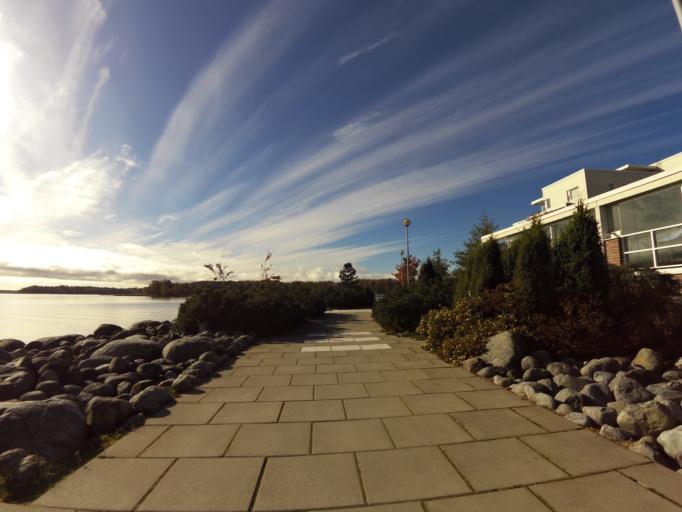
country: FI
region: Uusimaa
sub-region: Helsinki
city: Espoo
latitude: 60.1516
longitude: 24.6303
